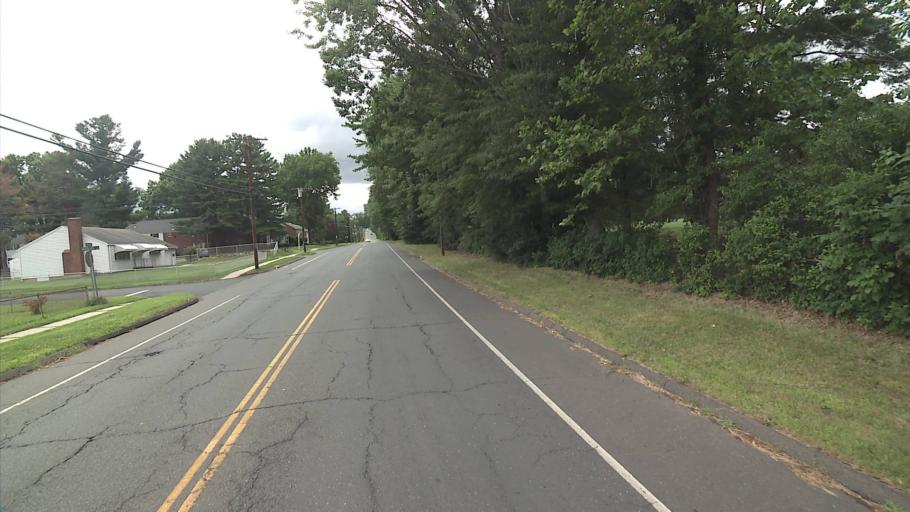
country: US
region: Connecticut
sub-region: Hartford County
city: Wethersfield
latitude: 41.7218
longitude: -72.6822
